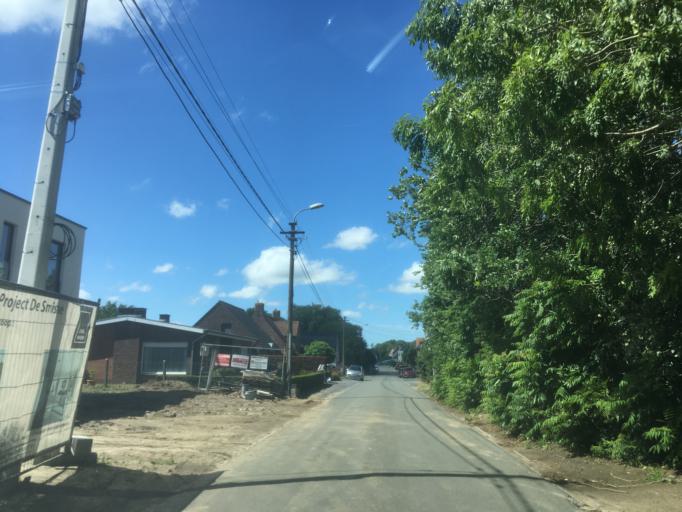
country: BE
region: Flanders
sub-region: Provincie West-Vlaanderen
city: Torhout
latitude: 51.0843
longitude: 3.0682
